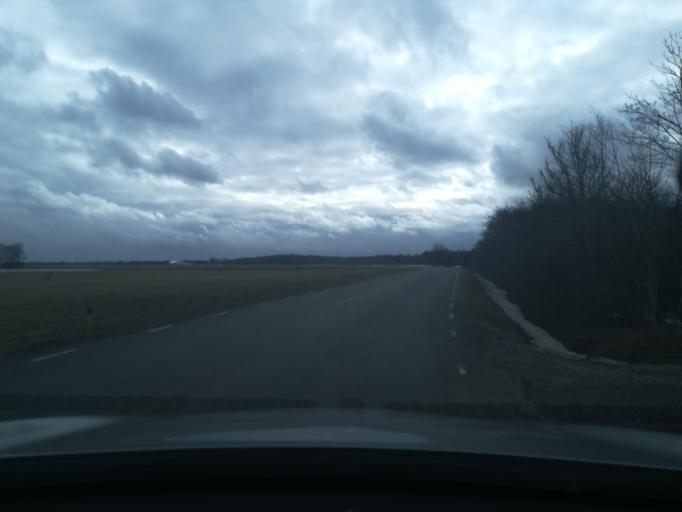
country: EE
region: Harju
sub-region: Saue linn
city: Saue
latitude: 59.3495
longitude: 24.5388
